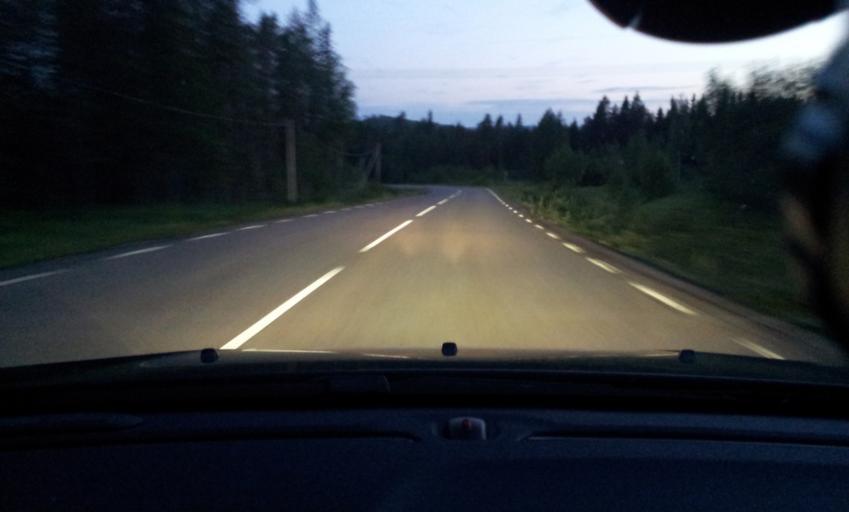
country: SE
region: Jaemtland
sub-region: Bergs Kommun
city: Hoverberg
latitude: 62.6562
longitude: 14.8300
